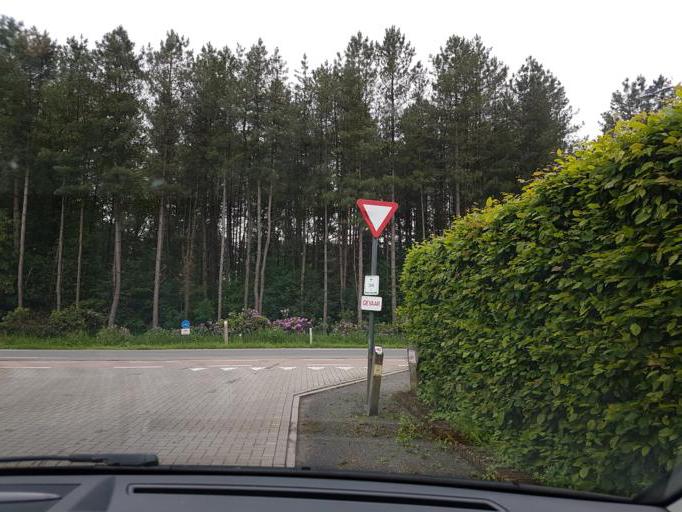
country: BE
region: Flanders
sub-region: Provincie Antwerpen
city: Merksplas
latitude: 51.3820
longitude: 4.8273
